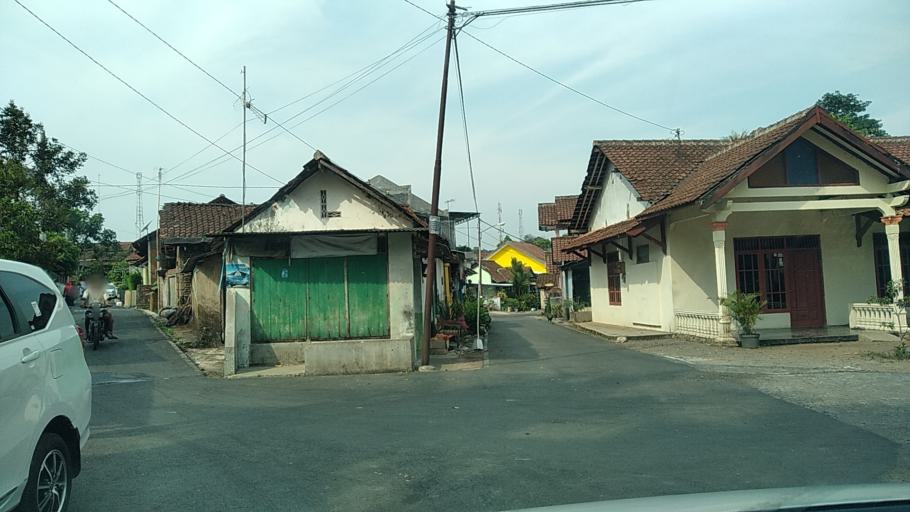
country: ID
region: Central Java
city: Ungaran
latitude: -7.1069
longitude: 110.3859
